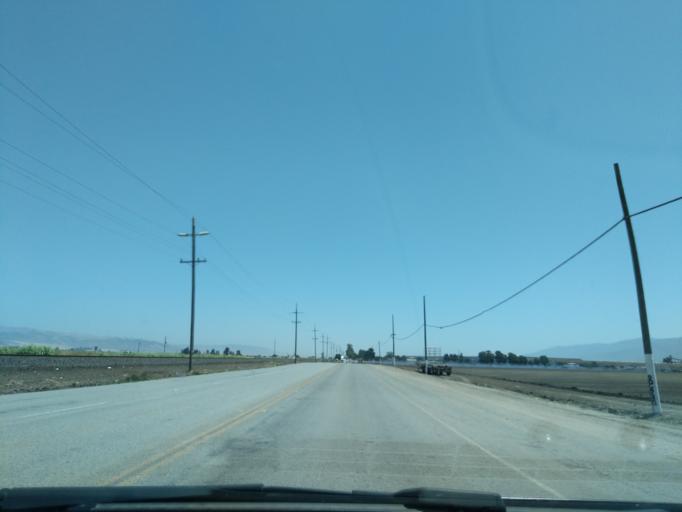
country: US
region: California
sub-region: Monterey County
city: Salinas
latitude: 36.6343
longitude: -121.5976
